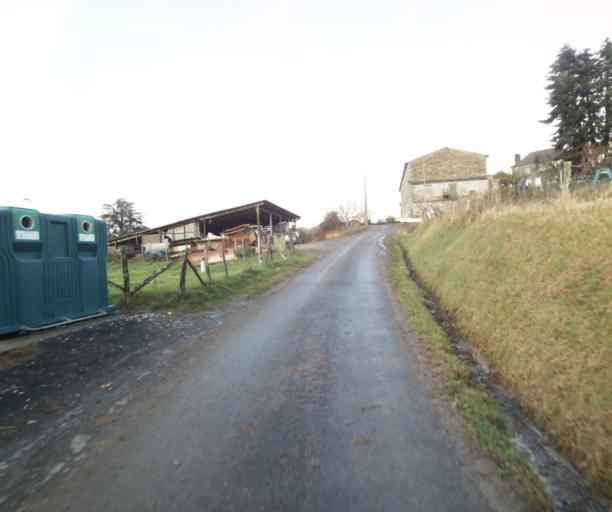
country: FR
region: Limousin
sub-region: Departement de la Correze
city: Cornil
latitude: 45.2185
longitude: 1.6707
